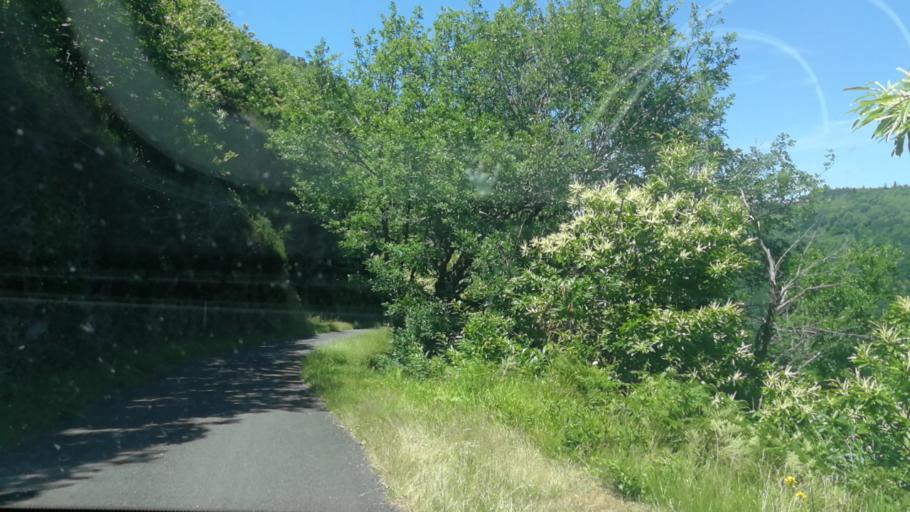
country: FR
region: Midi-Pyrenees
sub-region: Departement de l'Aveyron
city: Firmi
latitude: 44.5928
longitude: 2.3928
